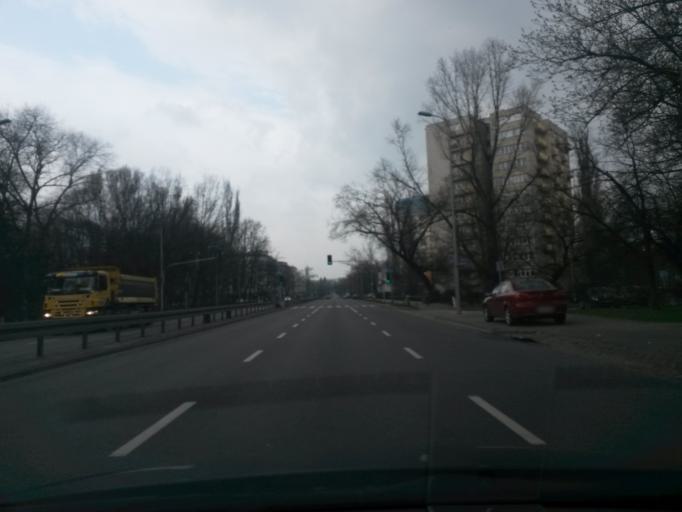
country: PL
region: Masovian Voivodeship
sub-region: Warszawa
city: Mokotow
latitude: 52.2036
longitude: 21.0339
